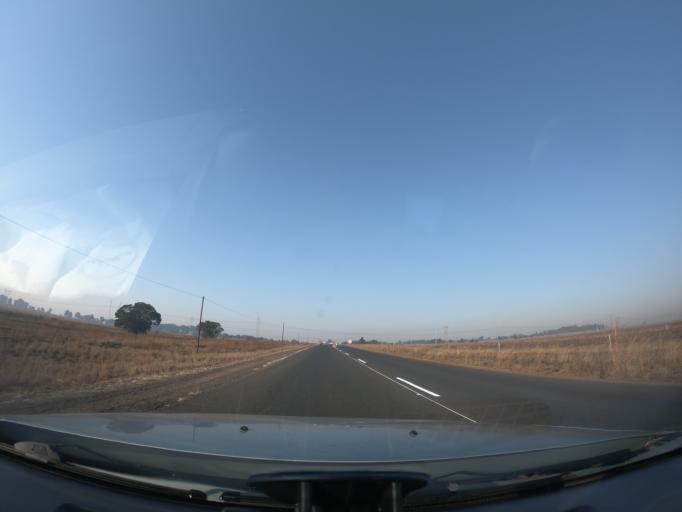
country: ZA
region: Mpumalanga
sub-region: Nkangala District Municipality
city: Middelburg
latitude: -25.8246
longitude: 29.4609
